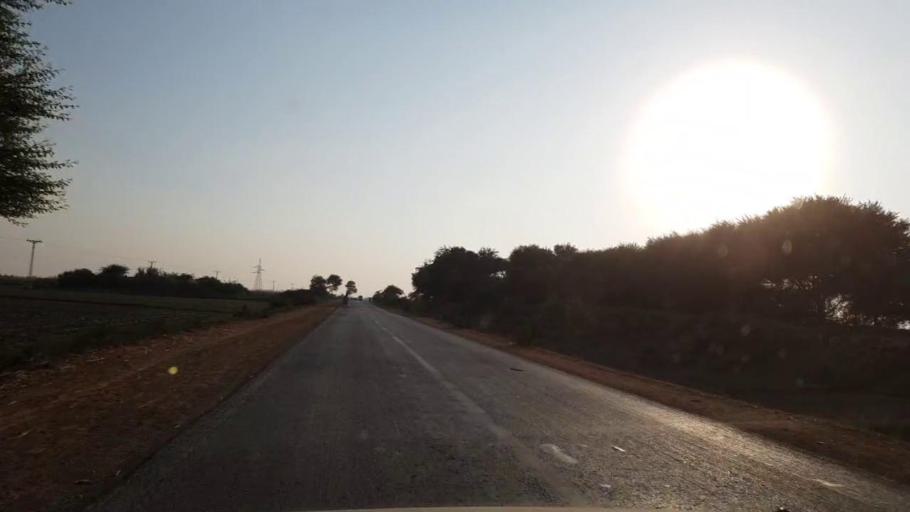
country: PK
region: Sindh
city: Daro Mehar
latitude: 24.6556
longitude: 68.1296
